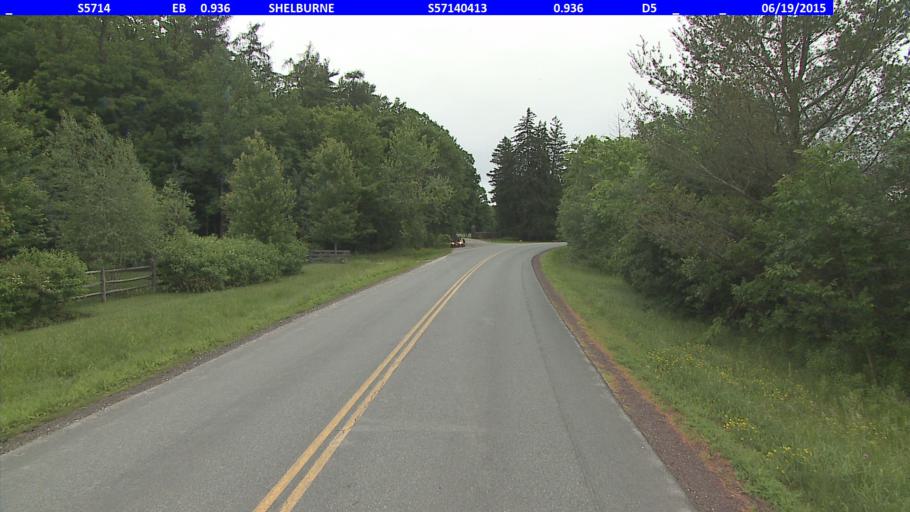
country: US
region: Vermont
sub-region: Chittenden County
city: Burlington
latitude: 44.3856
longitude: -73.2440
